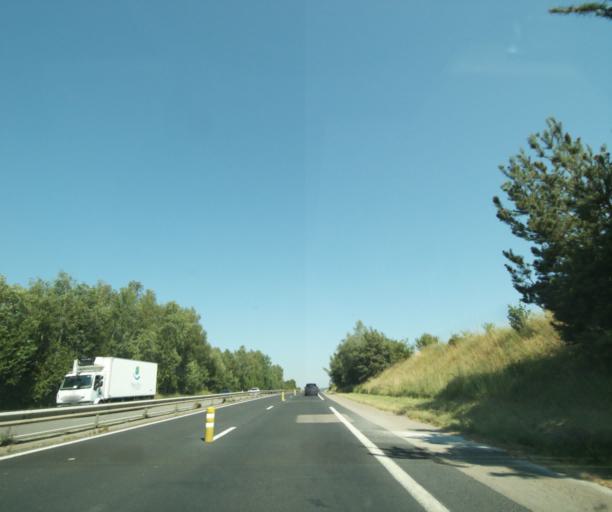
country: FR
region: Lorraine
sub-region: Departement de Meurthe-et-Moselle
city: Domgermain
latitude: 48.6564
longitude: 5.8414
